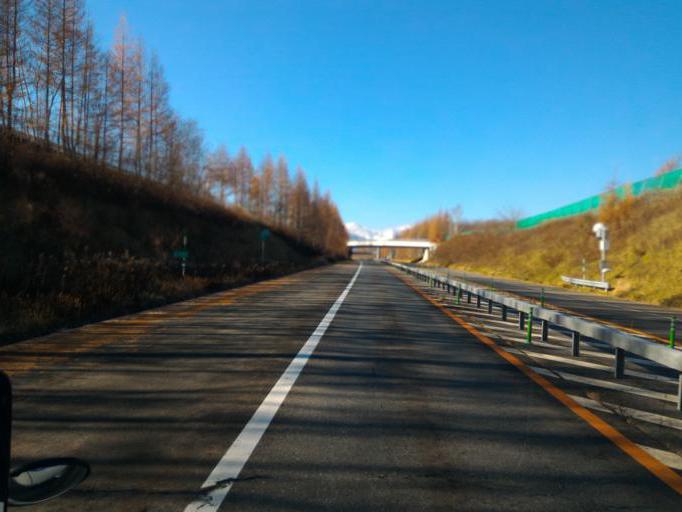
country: JP
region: Hokkaido
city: Otofuke
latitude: 42.9778
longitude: 142.9305
